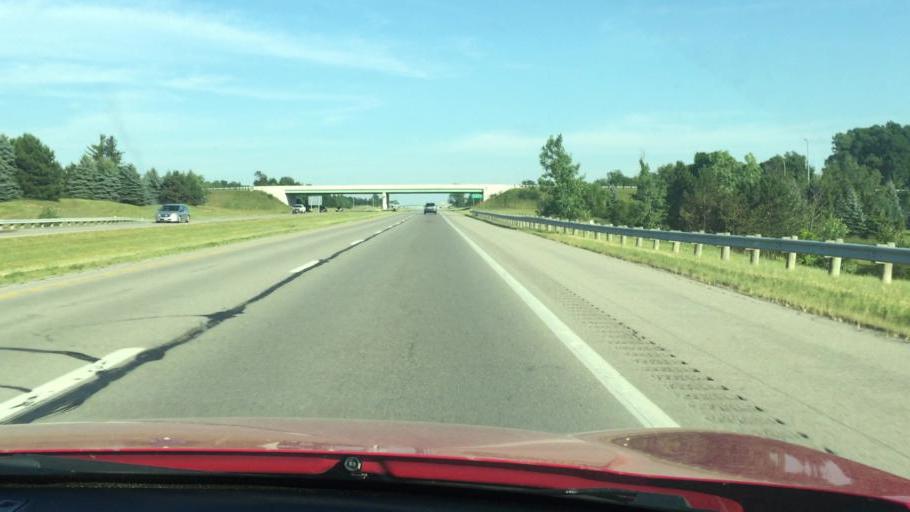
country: US
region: Ohio
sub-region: Logan County
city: Bellefontaine
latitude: 40.3704
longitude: -83.7326
